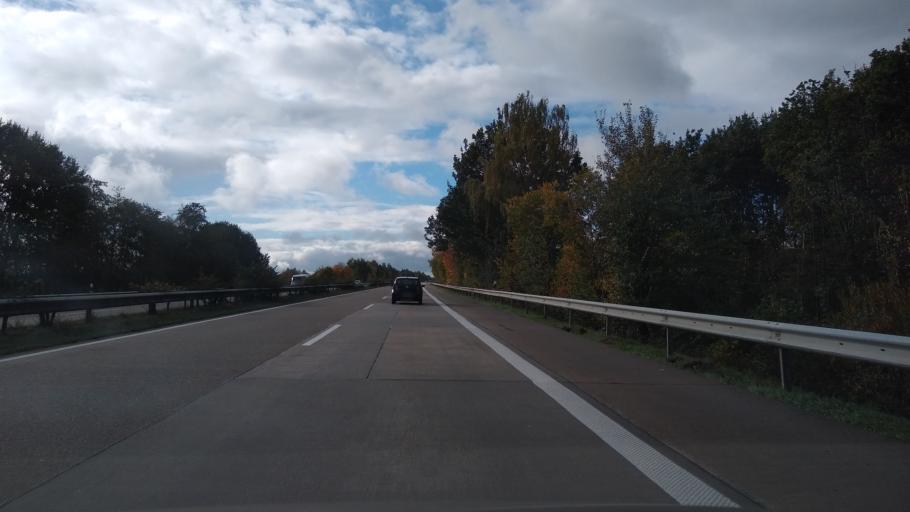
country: DE
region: Lower Saxony
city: Wardenburg
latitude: 53.0856
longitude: 8.2570
